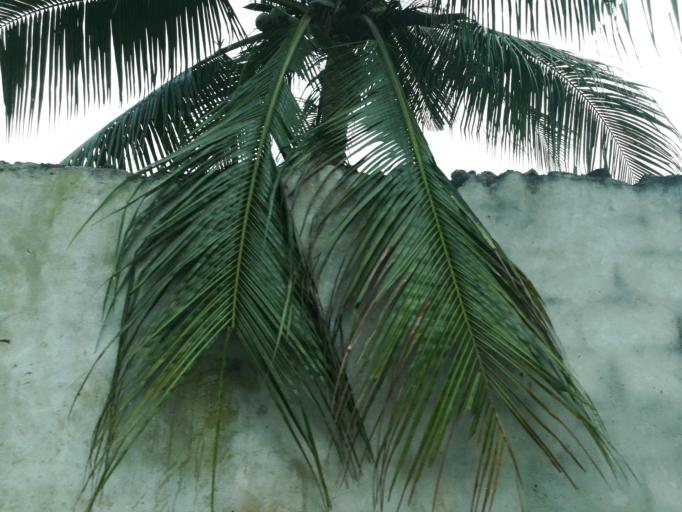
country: NG
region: Rivers
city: Port Harcourt
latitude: 4.8424
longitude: 7.0377
